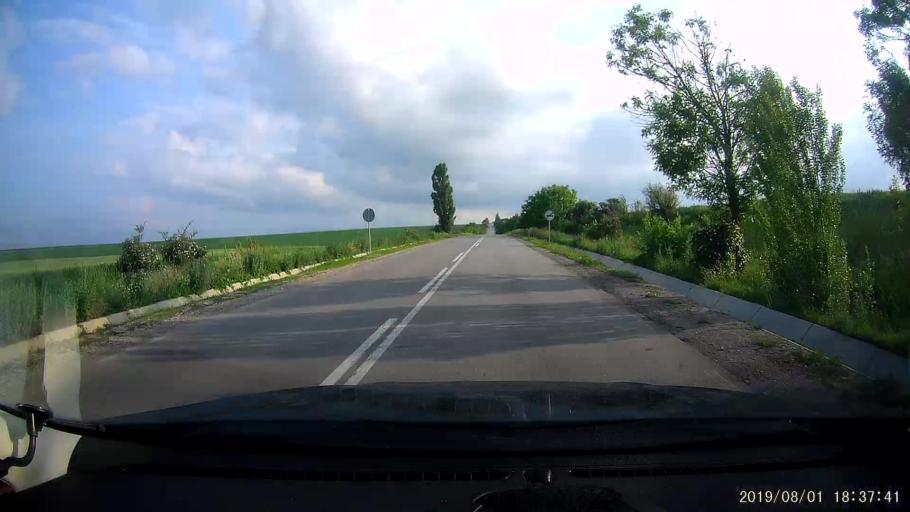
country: BG
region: Shumen
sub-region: Obshtina Khitrino
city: Gara Khitrino
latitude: 43.4160
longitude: 26.9270
